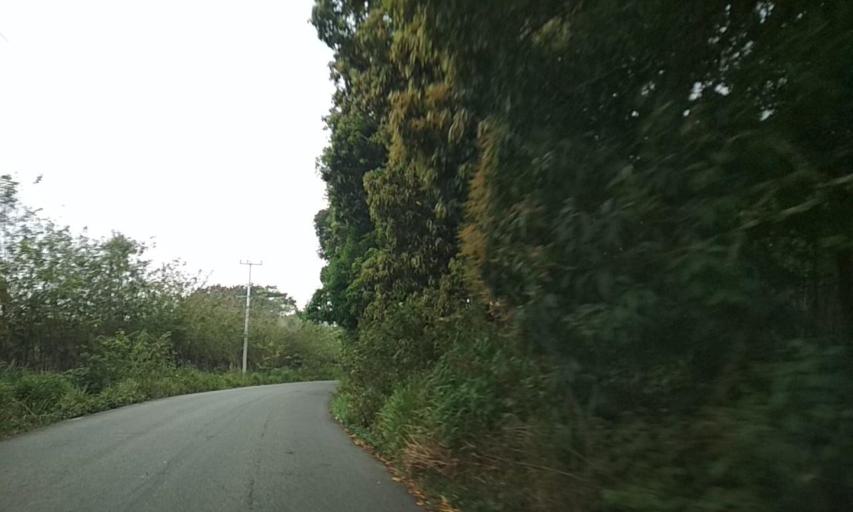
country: MX
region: Veracruz
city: Las Choapas
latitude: 17.8121
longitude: -94.1098
